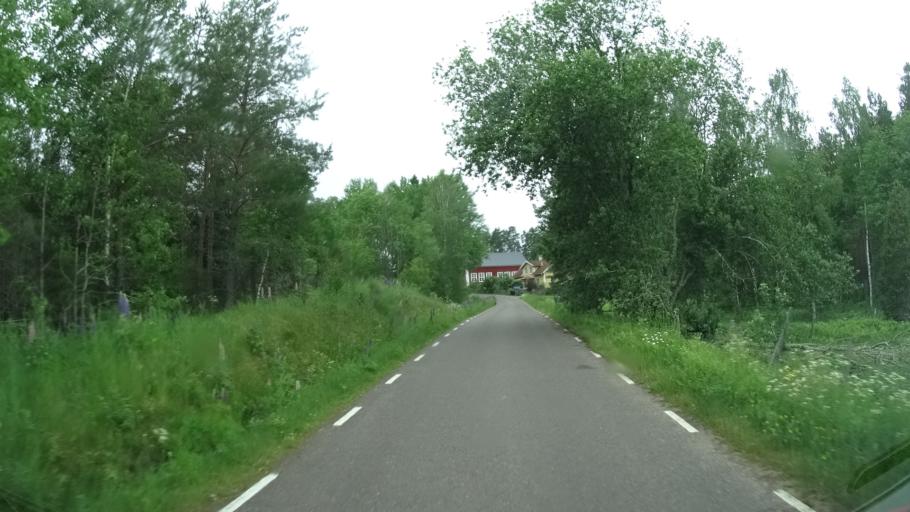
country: SE
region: Kalmar
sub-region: Vimmerby Kommun
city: Sodra Vi
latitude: 57.6926
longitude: 15.7022
